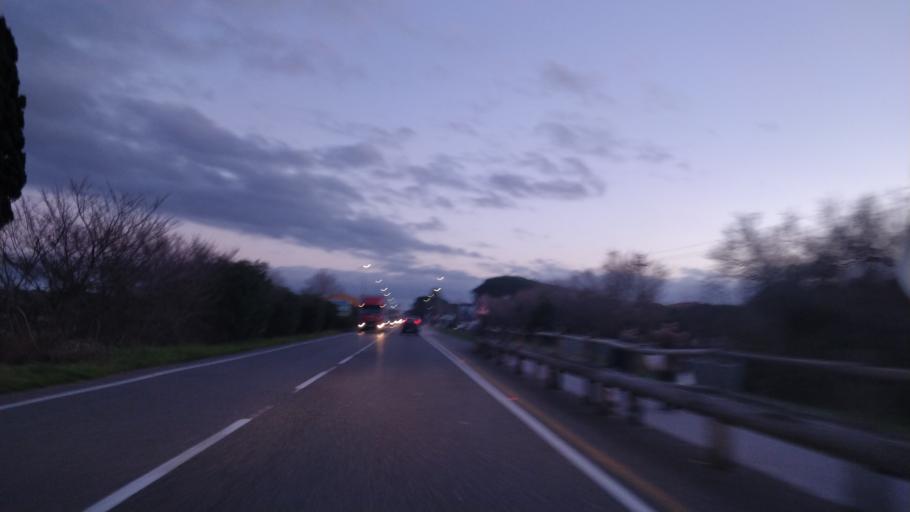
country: IT
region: Tuscany
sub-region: Provincia di Livorno
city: Vada
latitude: 43.3600
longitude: 10.4537
